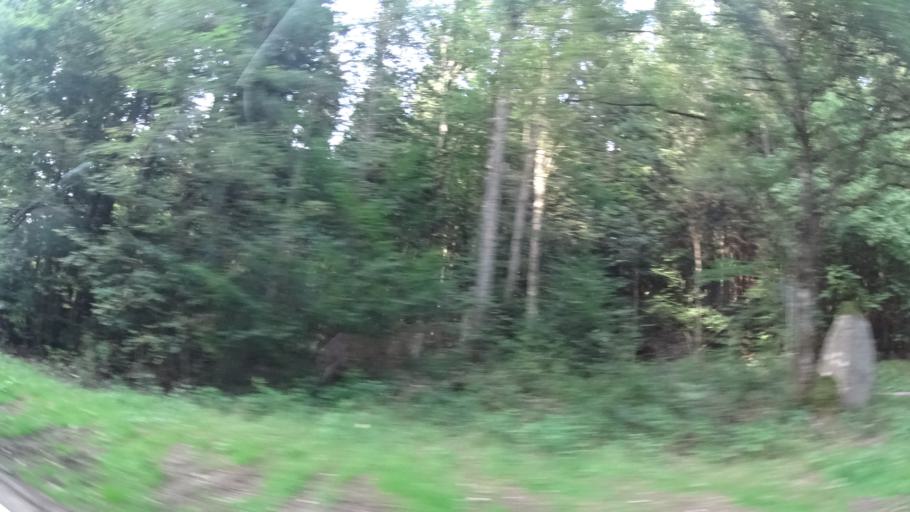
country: DE
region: Hesse
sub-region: Regierungsbezirk Darmstadt
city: Rothenberg
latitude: 49.5546
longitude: 8.8979
